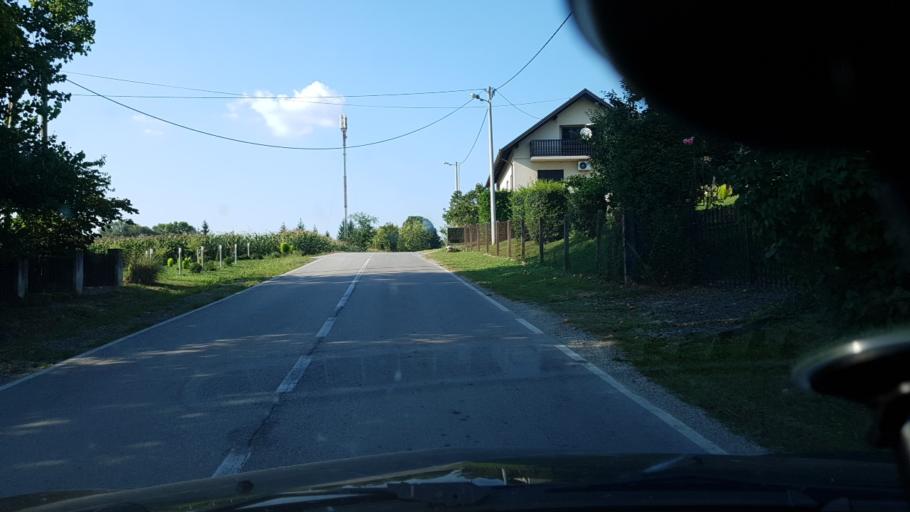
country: HR
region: Zagrebacka
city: Pojatno
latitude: 45.9652
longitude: 15.7370
